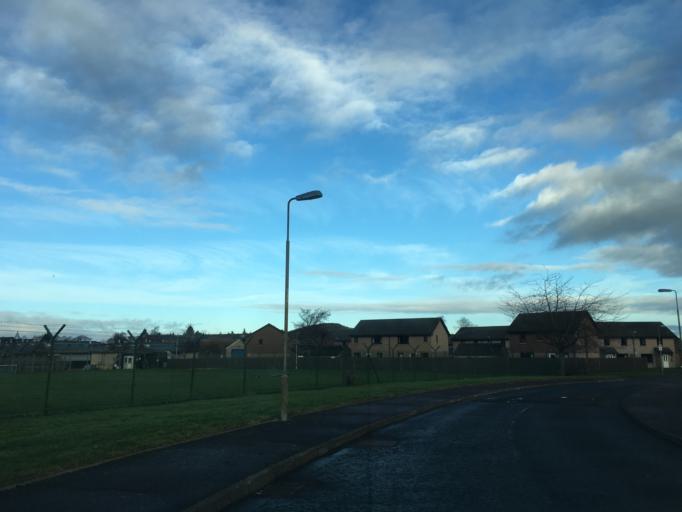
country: GB
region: Scotland
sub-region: Edinburgh
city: Colinton
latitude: 55.9076
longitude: -3.2435
